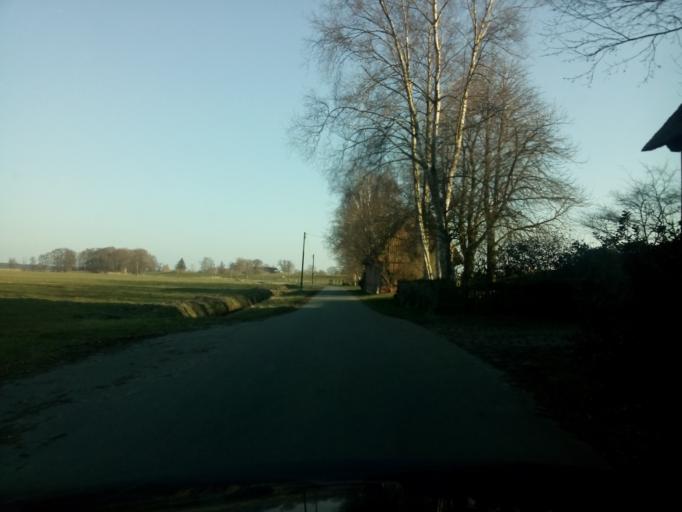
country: DE
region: Lower Saxony
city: Osterholz-Scharmbeck
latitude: 53.1598
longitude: 8.8330
